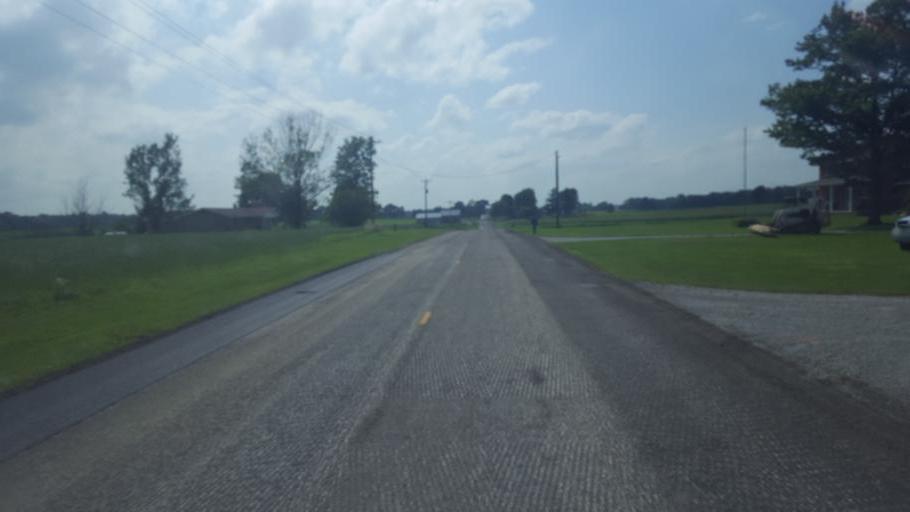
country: US
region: Ohio
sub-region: Huron County
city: Willard
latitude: 40.9601
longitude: -82.7669
